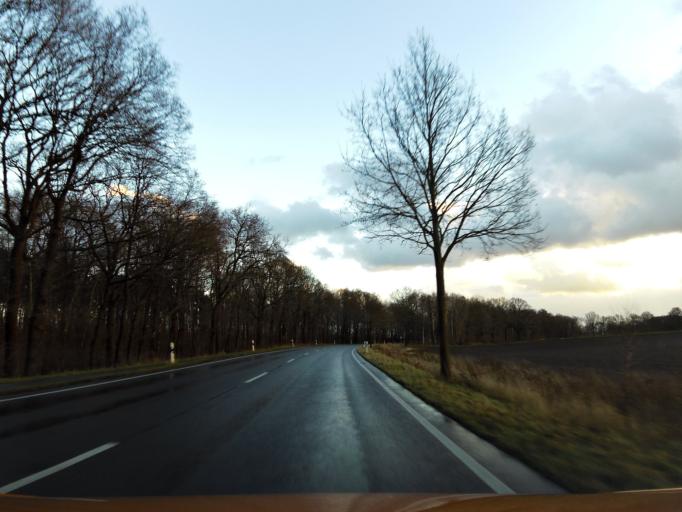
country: DE
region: Lower Saxony
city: Meinersen
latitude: 52.4409
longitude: 10.3253
